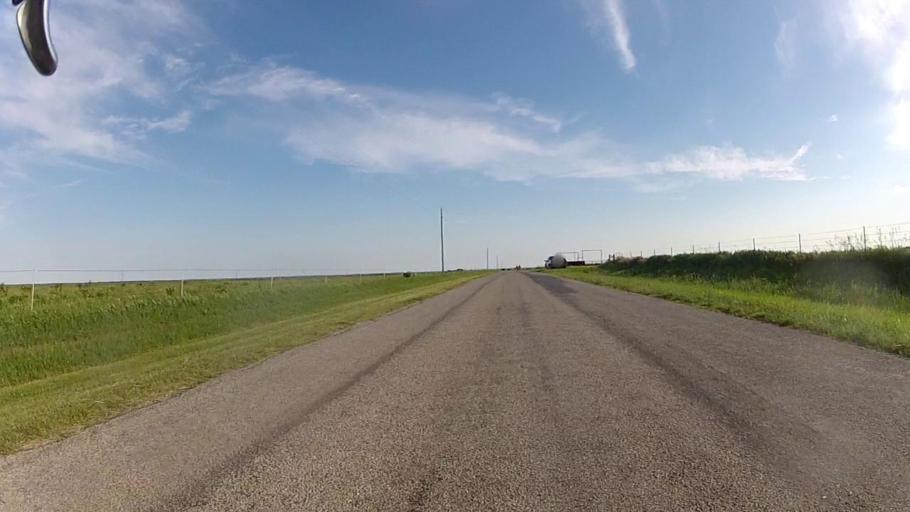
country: US
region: Kansas
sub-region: Cowley County
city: Arkansas City
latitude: 37.0526
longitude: -96.8230
